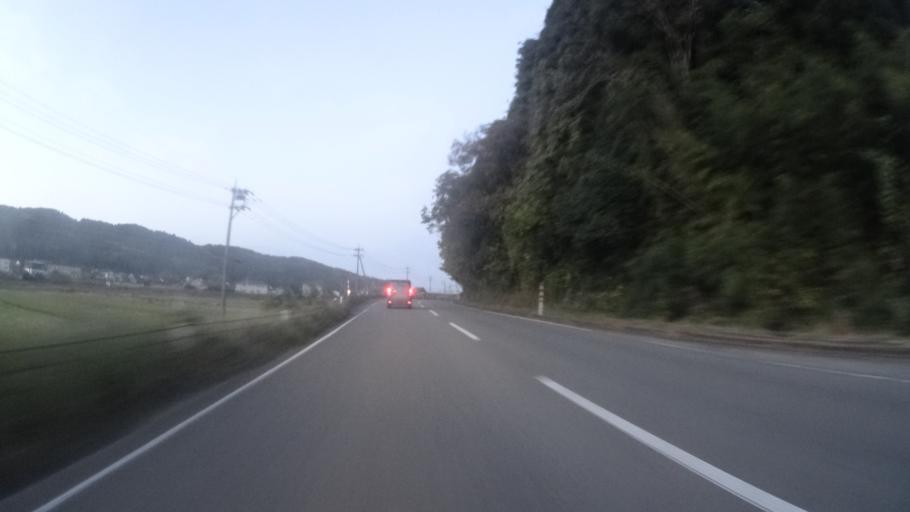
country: JP
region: Ishikawa
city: Nanao
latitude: 37.3741
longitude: 136.8796
